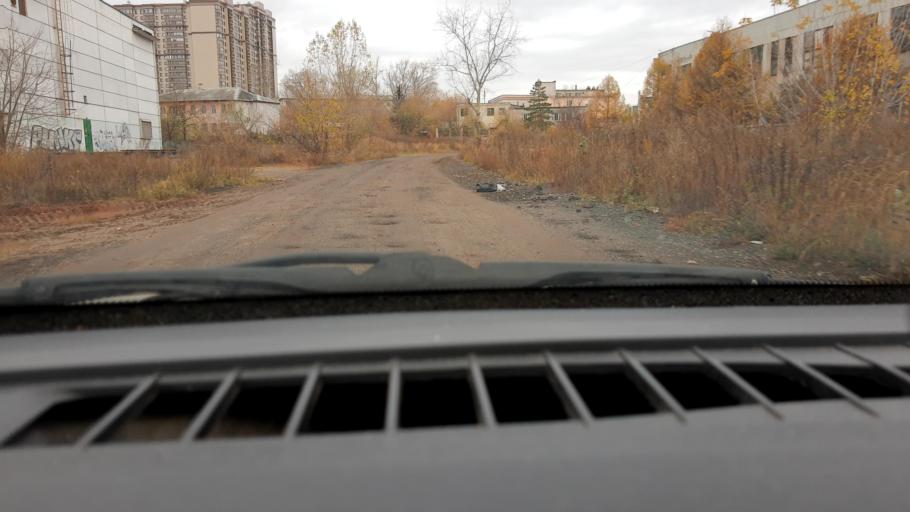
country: RU
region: Nizjnij Novgorod
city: Nizhniy Novgorod
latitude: 56.3095
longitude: 43.9527
